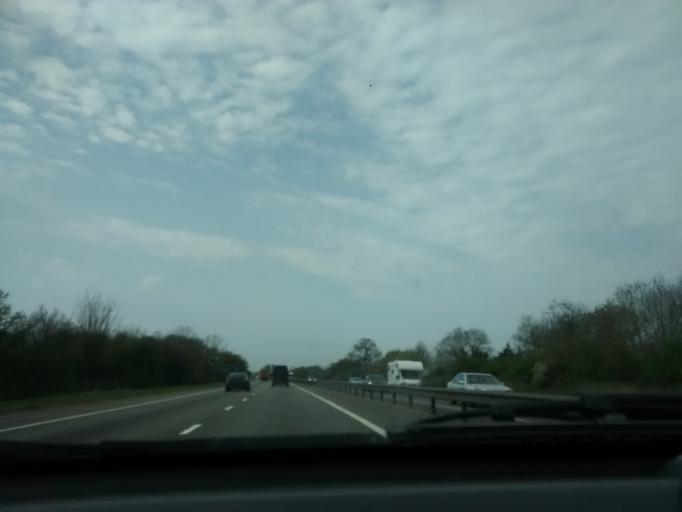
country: GB
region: England
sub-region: Oxfordshire
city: Kidlington
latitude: 51.8552
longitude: -1.2204
